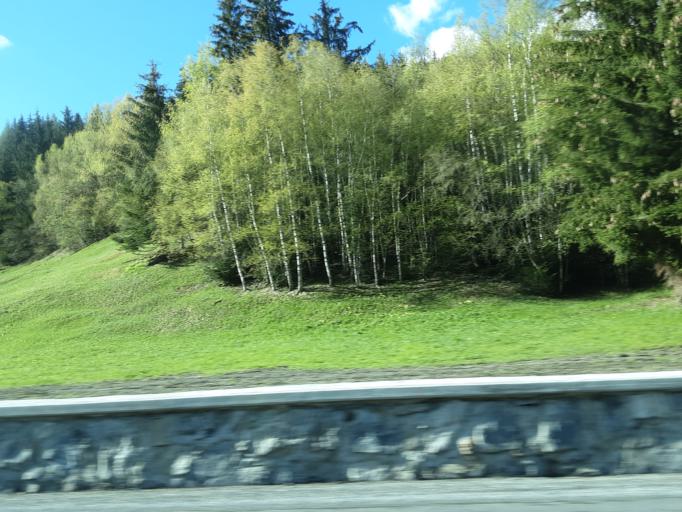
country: IT
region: Lombardy
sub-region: Provincia di Sondrio
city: Bormio
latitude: 46.4791
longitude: 10.3413
